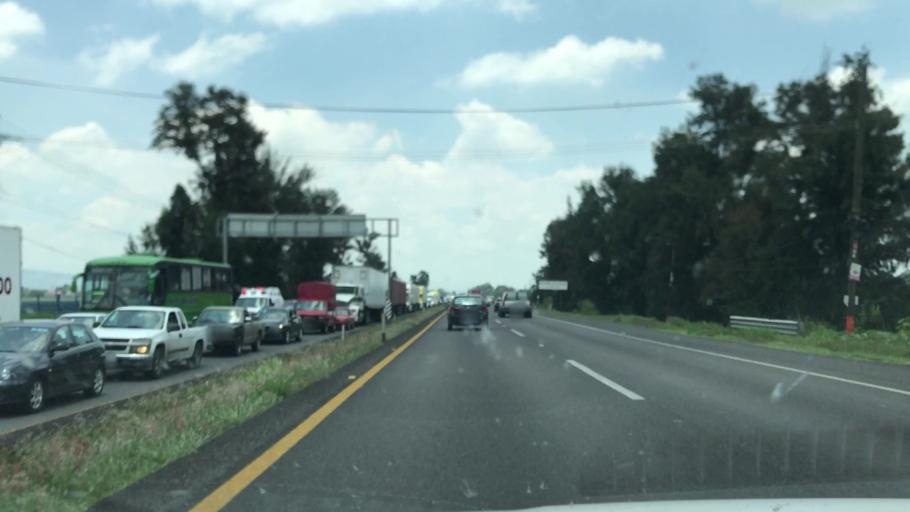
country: MX
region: Guanajuato
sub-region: Irapuato
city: Colonia Morelos de Guadalupe de Rivera
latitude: 20.5987
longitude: -101.4187
